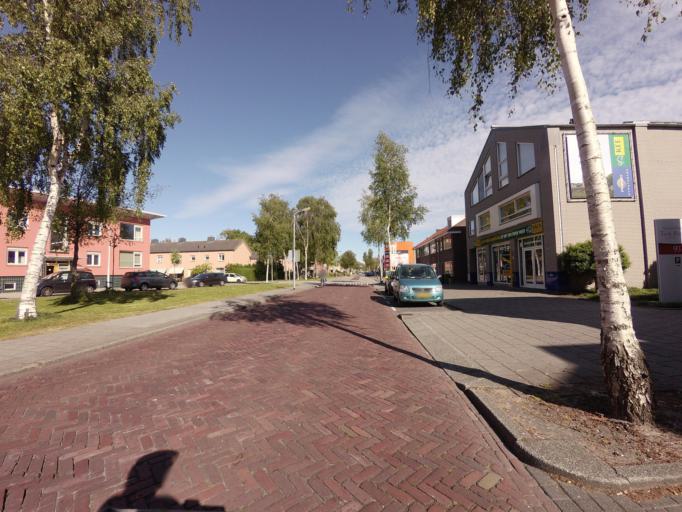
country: NL
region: North Holland
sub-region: Gemeente Uitgeest
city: Uitgeest
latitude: 52.5017
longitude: 4.7624
